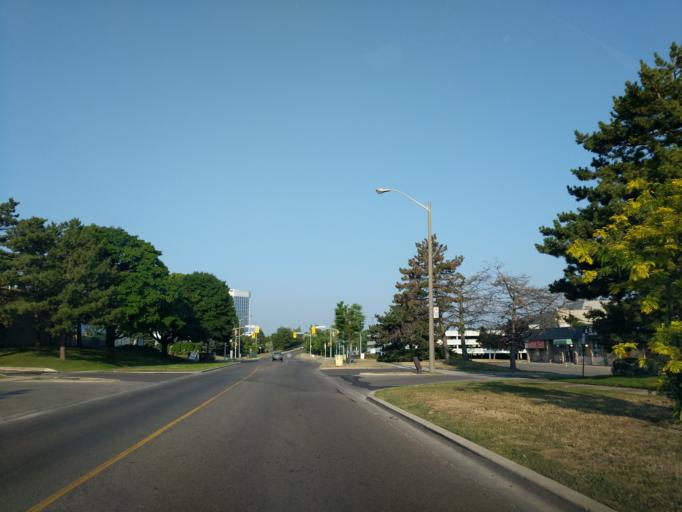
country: CA
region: Ontario
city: Willowdale
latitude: 43.8038
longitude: -79.3405
